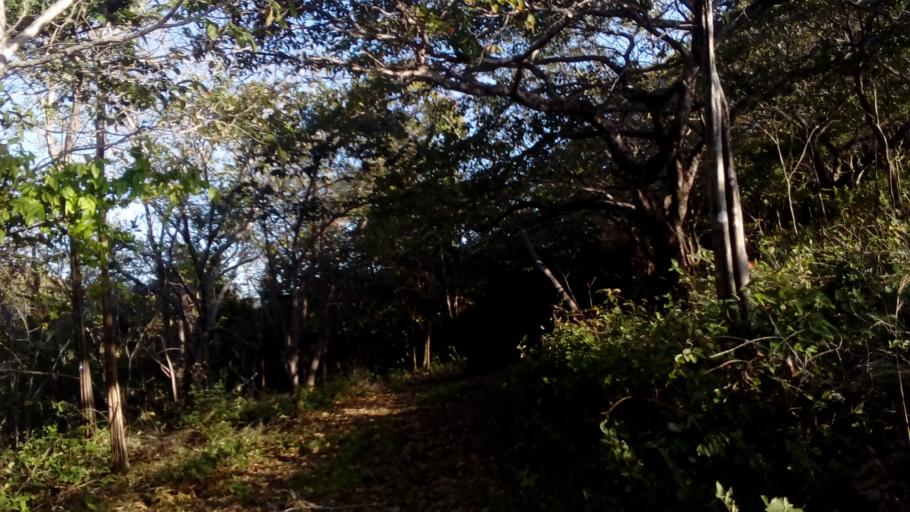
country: CR
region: Guanacaste
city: Sardinal
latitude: 10.3945
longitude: -85.8327
